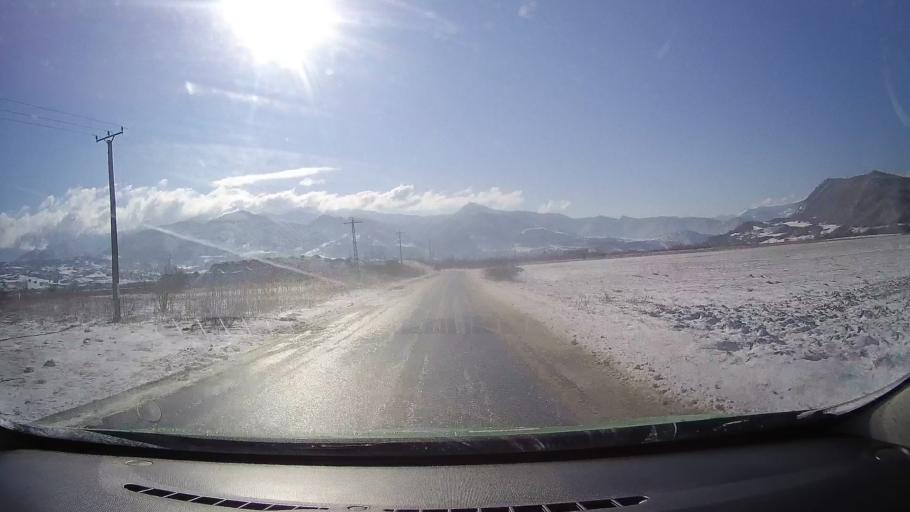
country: RO
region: Sibiu
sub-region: Comuna Turnu Rosu
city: Turnu Rosu
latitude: 45.6578
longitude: 24.2970
